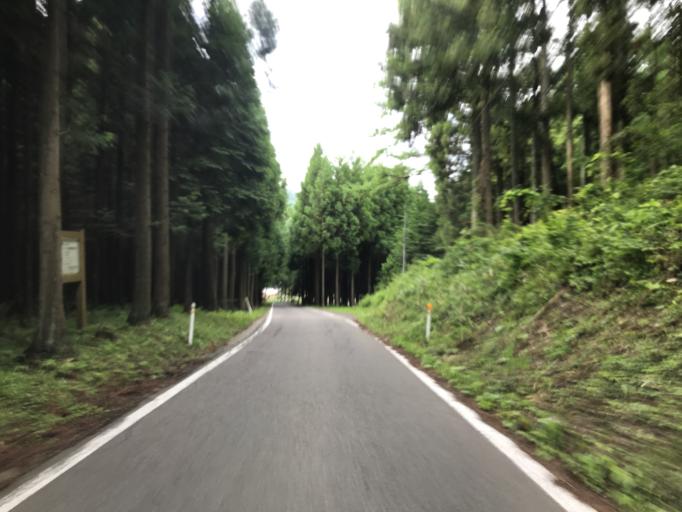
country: JP
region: Fukushima
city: Funehikimachi-funehiki
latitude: 37.4694
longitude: 140.6408
